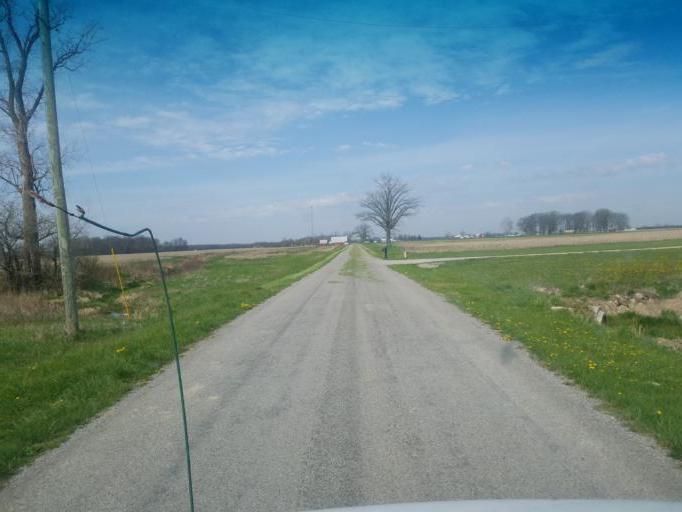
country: US
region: Ohio
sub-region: Union County
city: Richwood
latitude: 40.4829
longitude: -83.4625
